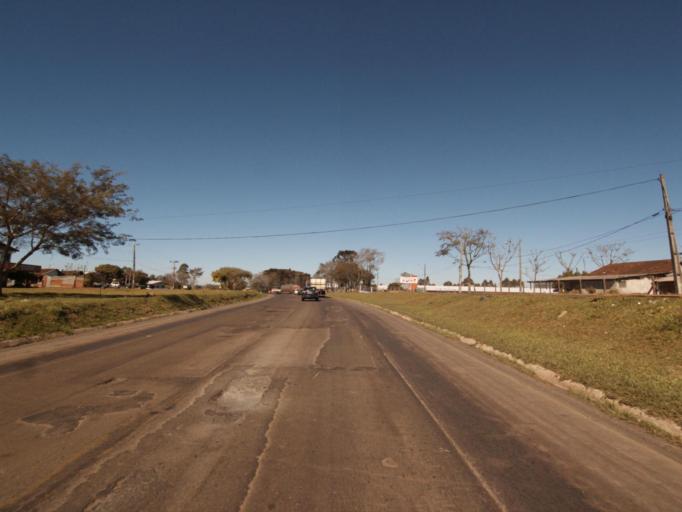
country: BR
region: Santa Catarina
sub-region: Chapeco
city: Chapeco
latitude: -26.8586
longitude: -52.9796
